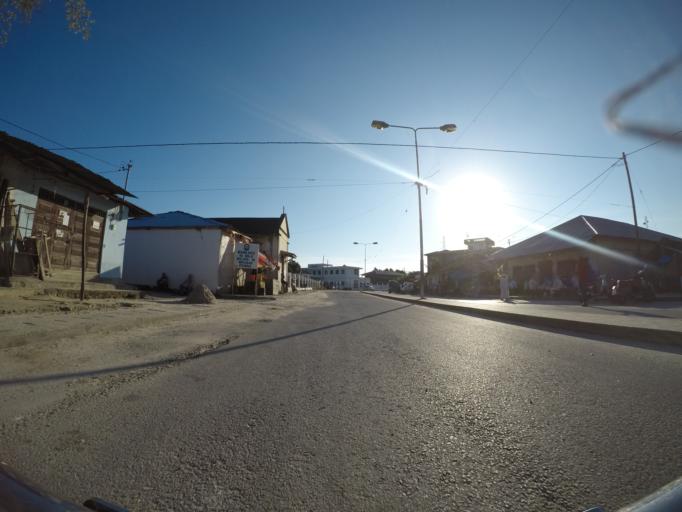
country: TZ
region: Pemba South
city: Uwelini
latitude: -5.3620
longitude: 39.6538
